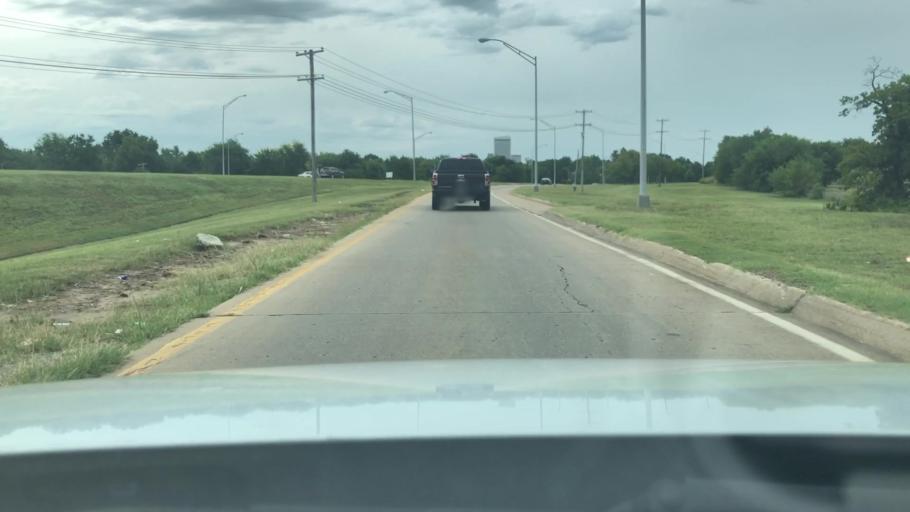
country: US
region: Oklahoma
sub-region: Tulsa County
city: Tulsa
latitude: 36.1760
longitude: -96.0017
